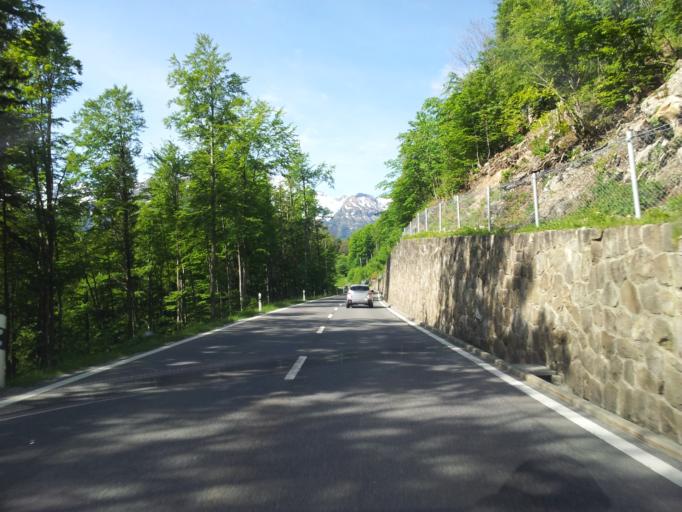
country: CH
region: Obwalden
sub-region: Obwalden
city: Lungern
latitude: 46.7629
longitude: 8.1431
